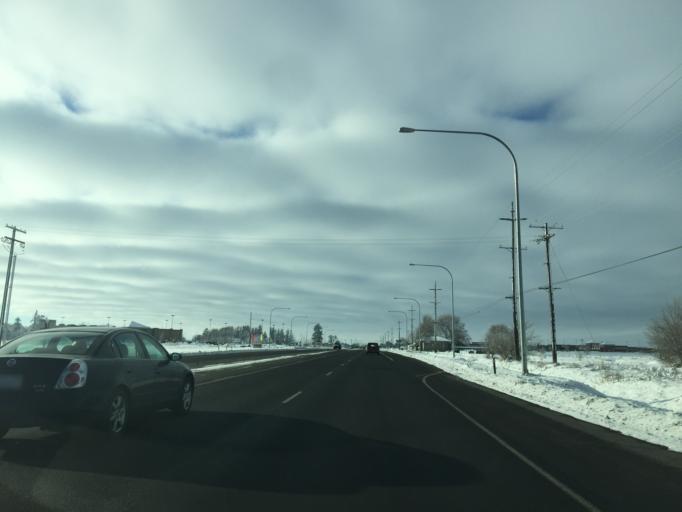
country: US
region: Washington
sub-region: Spokane County
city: Airway Heights
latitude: 47.6432
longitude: -117.5475
